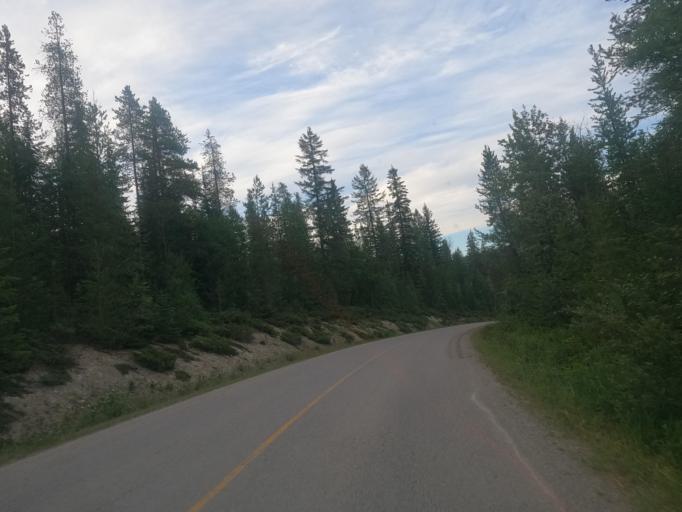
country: CA
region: British Columbia
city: Golden
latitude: 51.4289
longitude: -117.0441
